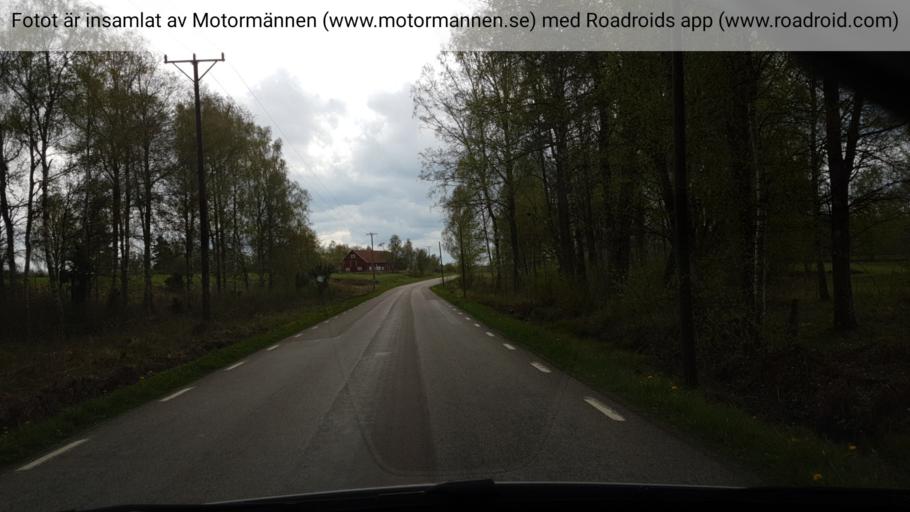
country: SE
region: Vaestra Goetaland
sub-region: Falkopings Kommun
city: Floby
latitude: 58.1676
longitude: 13.3426
